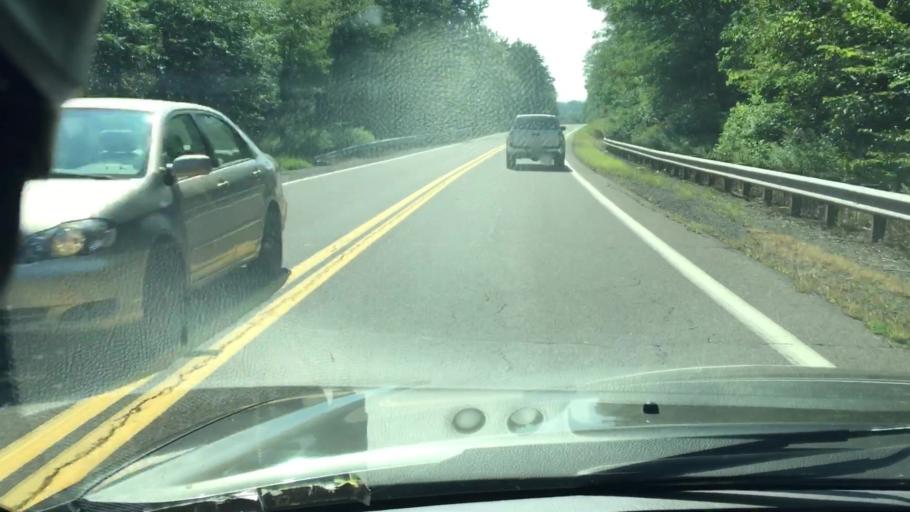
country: US
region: Pennsylvania
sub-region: Luzerne County
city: Nanticoke
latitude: 41.1890
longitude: -75.9683
